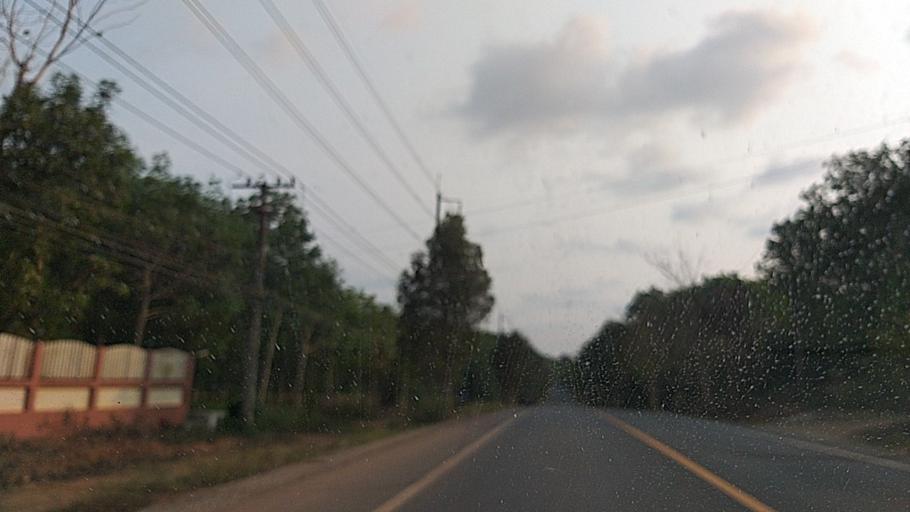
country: TH
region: Trat
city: Khao Saming
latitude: 12.3555
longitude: 102.3818
